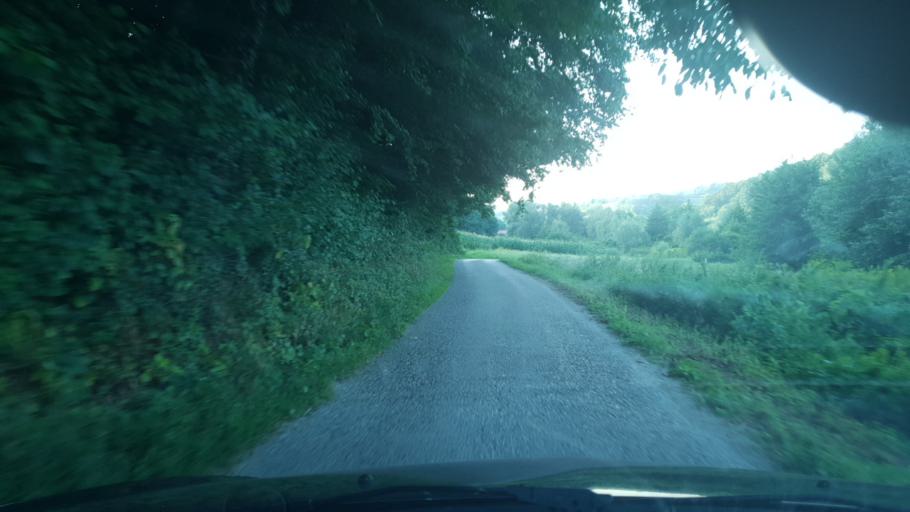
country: HR
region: Krapinsko-Zagorska
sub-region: Grad Krapina
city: Krapina
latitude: 46.1400
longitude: 15.8591
